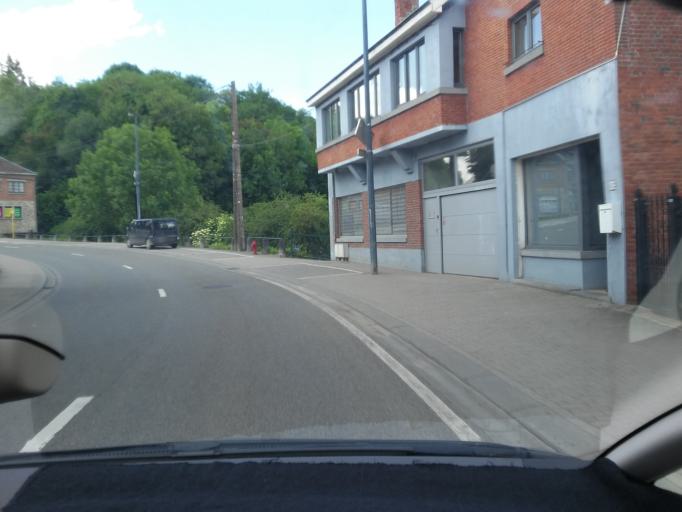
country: BE
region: Wallonia
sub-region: Province de Namur
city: Rochefort
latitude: 50.1629
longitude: 5.2192
